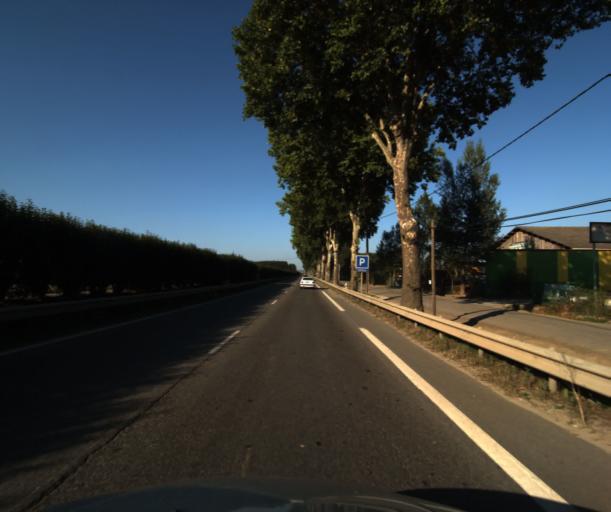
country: FR
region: Midi-Pyrenees
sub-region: Departement de la Haute-Garonne
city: Roquettes
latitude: 43.5004
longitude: 1.3537
